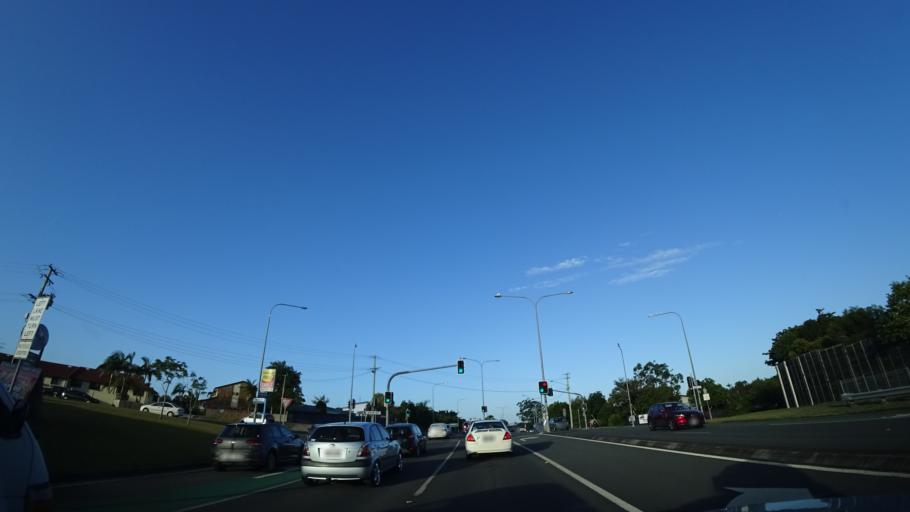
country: AU
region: Queensland
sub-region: Sunshine Coast
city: Buderim
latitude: -26.6563
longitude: 153.0718
